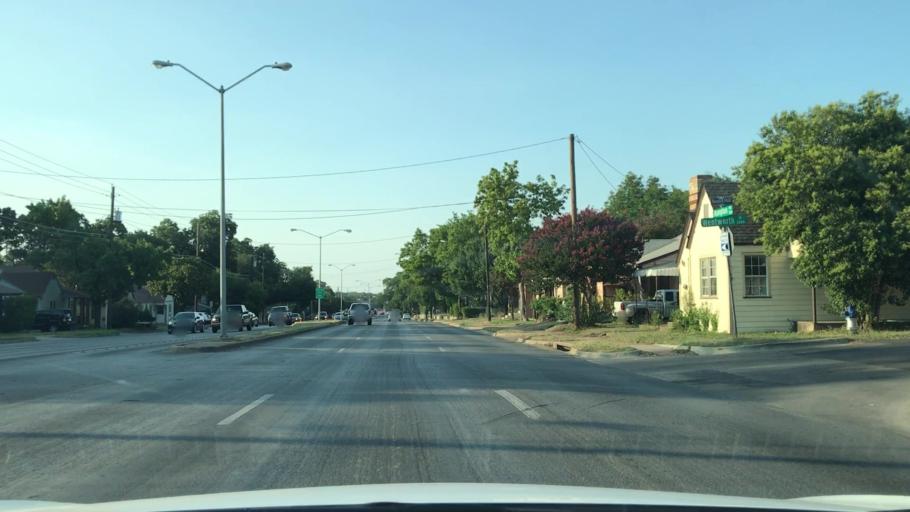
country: US
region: Texas
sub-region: Dallas County
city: Cockrell Hill
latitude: 32.7430
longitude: -96.8568
